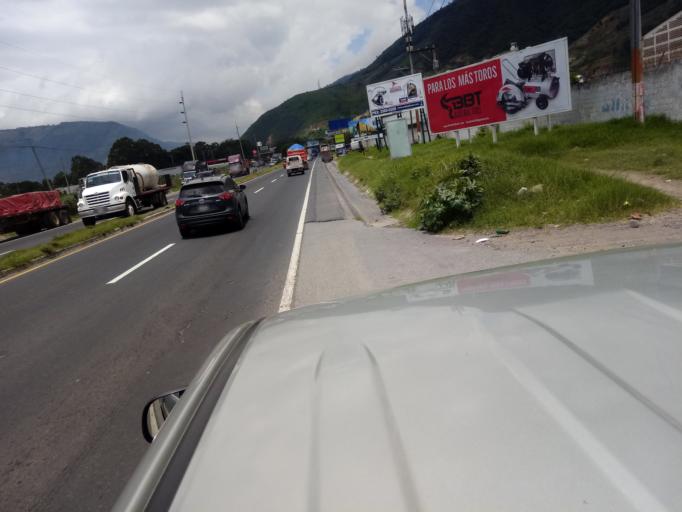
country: GT
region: Guatemala
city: Amatitlan
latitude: 14.4689
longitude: -90.6379
